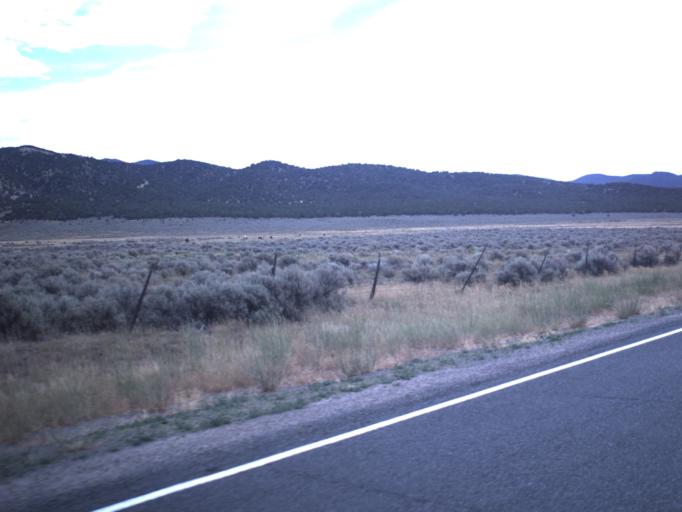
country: US
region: Utah
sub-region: Beaver County
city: Beaver
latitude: 38.6084
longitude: -112.5942
